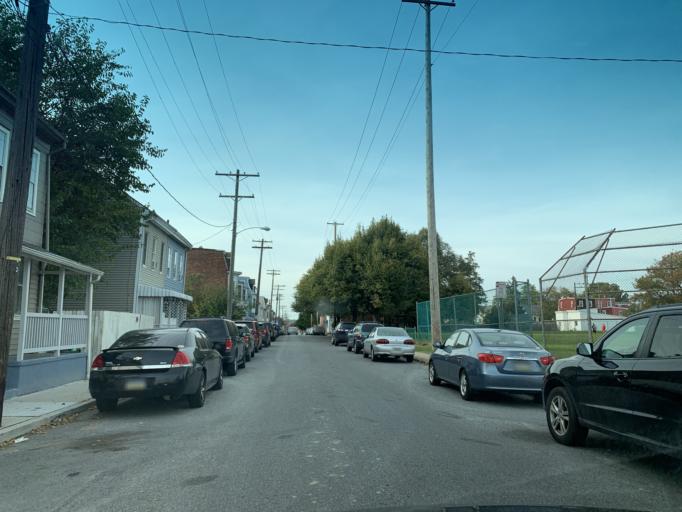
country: US
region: Pennsylvania
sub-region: York County
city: York
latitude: 39.9660
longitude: -76.7354
